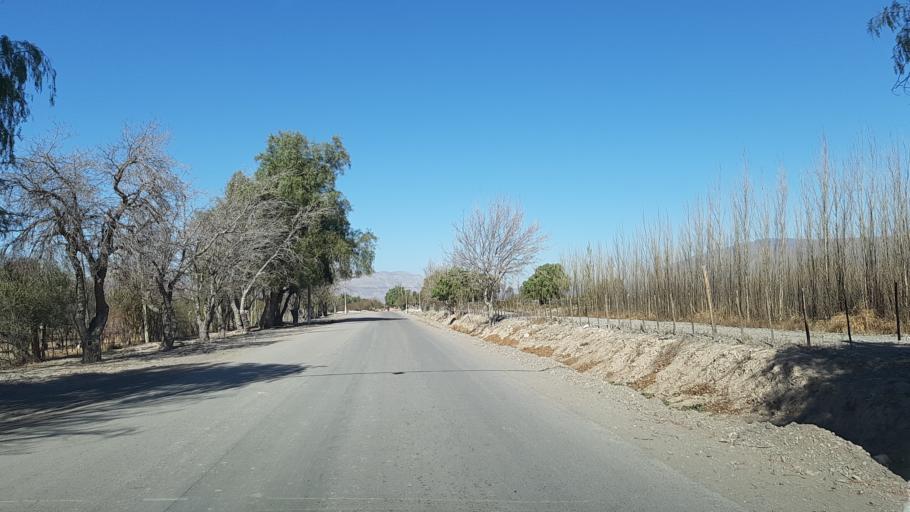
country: AR
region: San Juan
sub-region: Departamento de Zonda
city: Zonda
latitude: -31.4674
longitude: -68.7228
